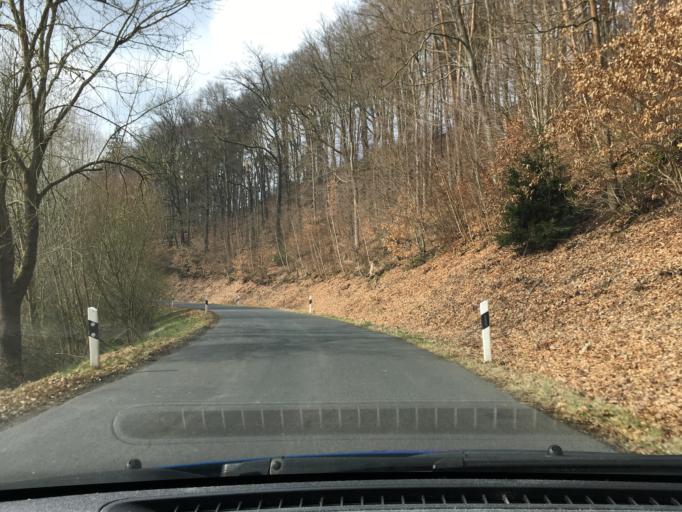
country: DE
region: Lower Saxony
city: Adelebsen
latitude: 51.5581
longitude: 9.7254
